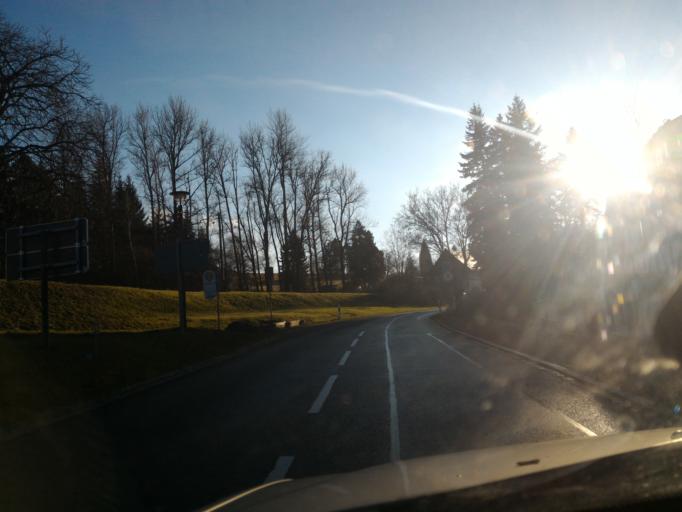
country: DE
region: Saxony
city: Kurort Jonsdorf
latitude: 50.8536
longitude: 14.7056
